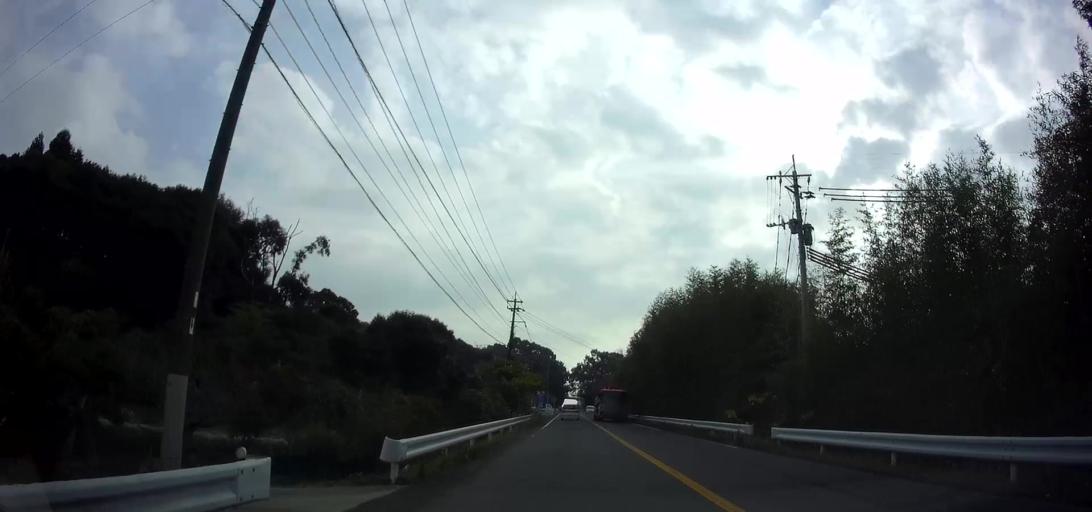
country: JP
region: Nagasaki
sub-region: Isahaya-shi
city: Isahaya
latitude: 32.7967
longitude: 130.0933
